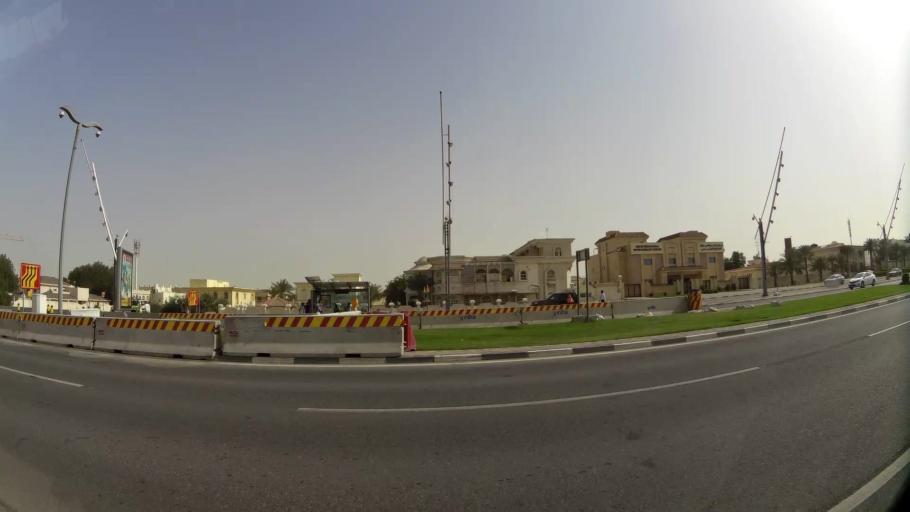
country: QA
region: Baladiyat ar Rayyan
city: Ar Rayyan
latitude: 25.2562
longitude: 51.4423
